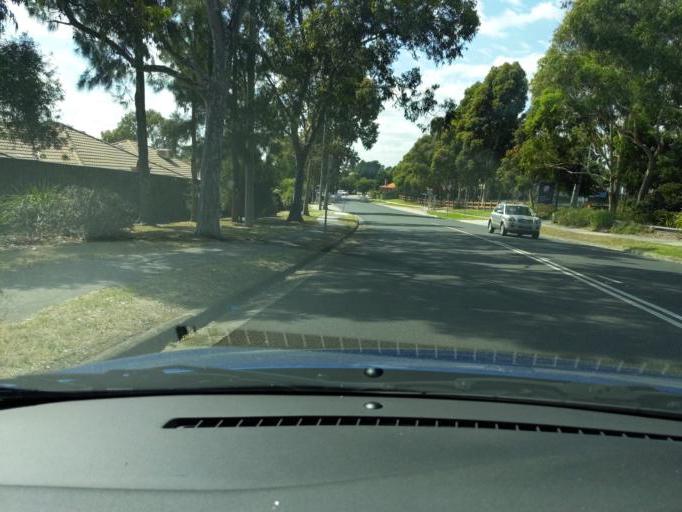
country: AU
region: Victoria
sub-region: Knox
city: Rowville
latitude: -37.9188
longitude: 145.2393
